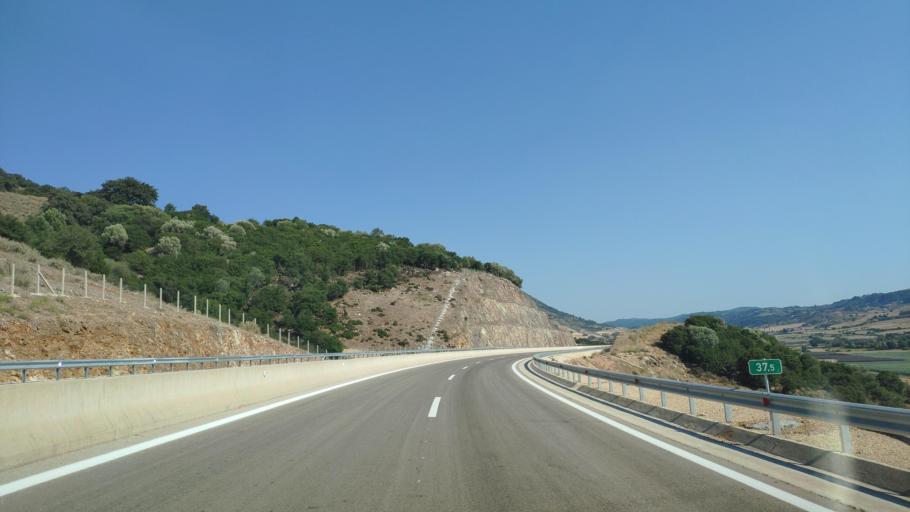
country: GR
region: West Greece
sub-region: Nomos Aitolias kai Akarnanias
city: Katouna
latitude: 38.8369
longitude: 21.1146
